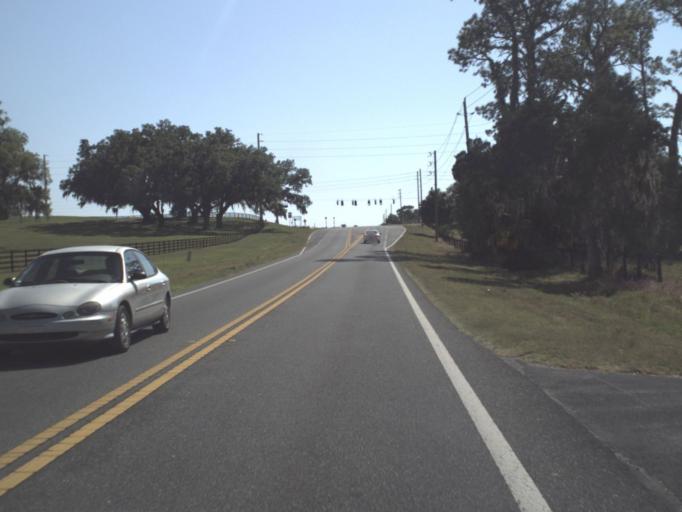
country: US
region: Florida
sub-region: Marion County
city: Dunnellon
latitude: 29.1596
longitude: -82.3494
